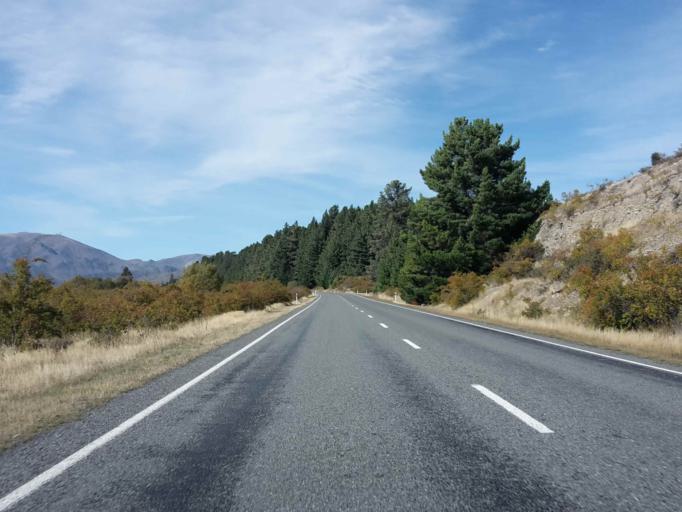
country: NZ
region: Otago
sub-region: Queenstown-Lakes District
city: Wanaka
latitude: -44.5114
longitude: 169.7922
